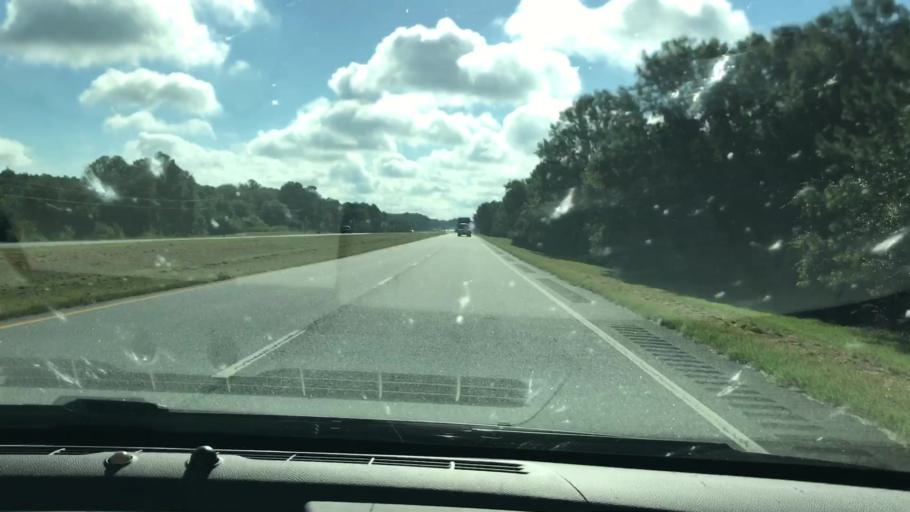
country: US
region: Georgia
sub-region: Worth County
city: Sylvester
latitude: 31.5539
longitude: -83.9855
